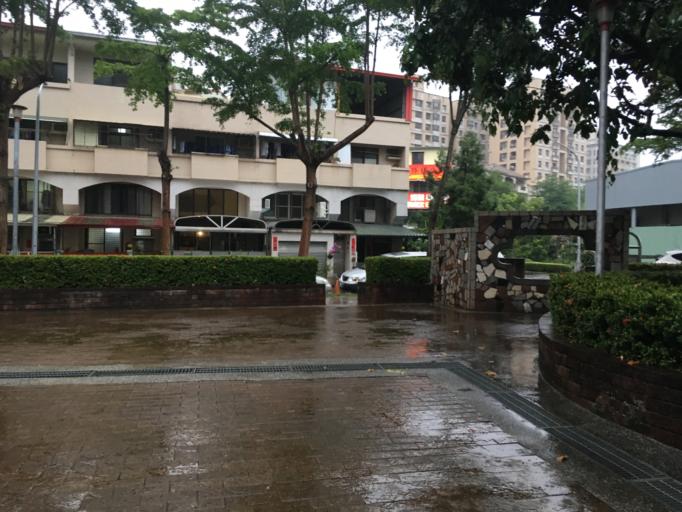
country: TW
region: Taiwan
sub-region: Taichung City
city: Taichung
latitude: 24.1741
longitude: 120.7128
